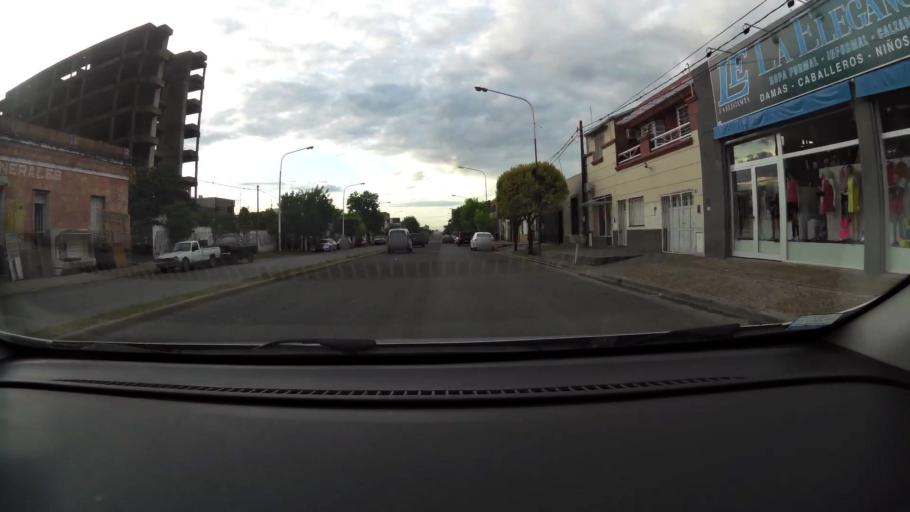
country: AR
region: Buenos Aires
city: San Nicolas de los Arroyos
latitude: -33.3336
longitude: -60.2262
